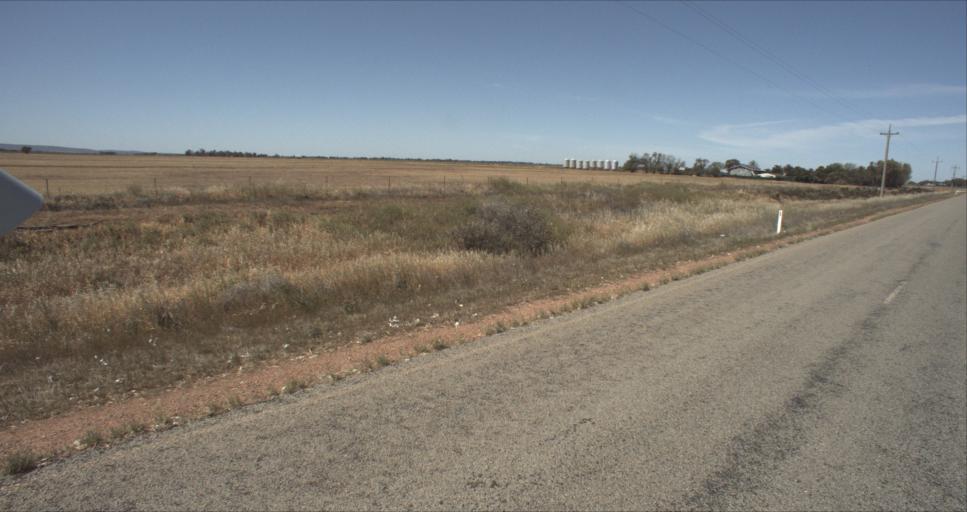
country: AU
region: New South Wales
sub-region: Leeton
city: Leeton
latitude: -34.4490
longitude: 146.2963
